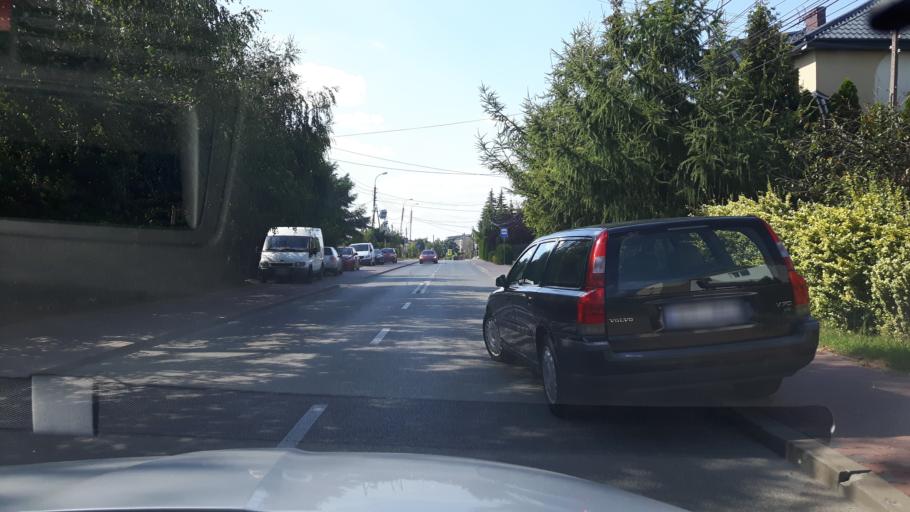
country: PL
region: Masovian Voivodeship
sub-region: Powiat pruszkowski
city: Raszyn
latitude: 52.1592
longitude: 20.9196
